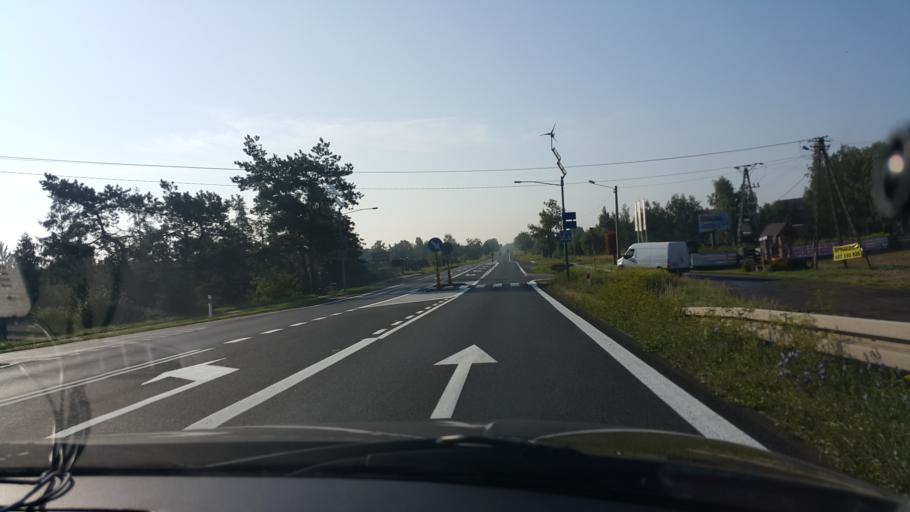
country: PL
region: Masovian Voivodeship
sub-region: Powiat radomski
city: Jastrzebia
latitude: 51.4098
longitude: 21.2403
